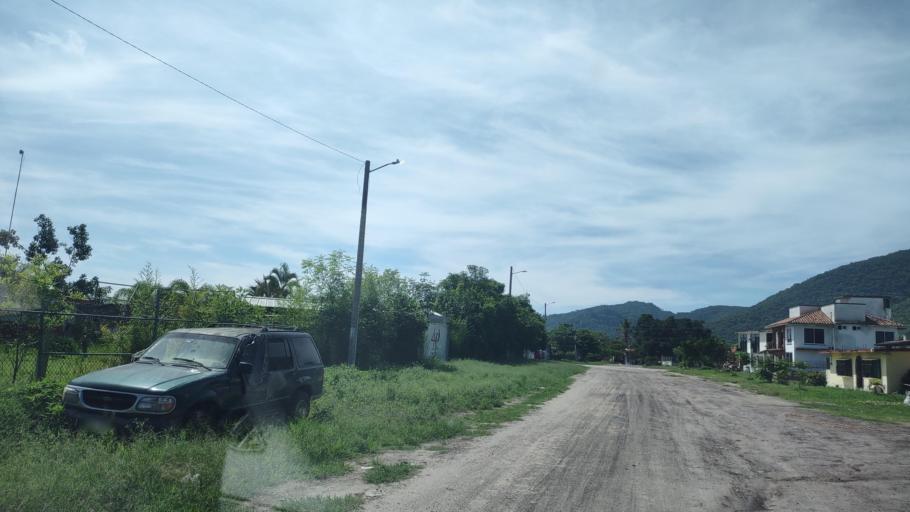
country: MX
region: Veracruz
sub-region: Emiliano Zapata
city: Dos Rios
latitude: 19.4282
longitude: -96.7982
